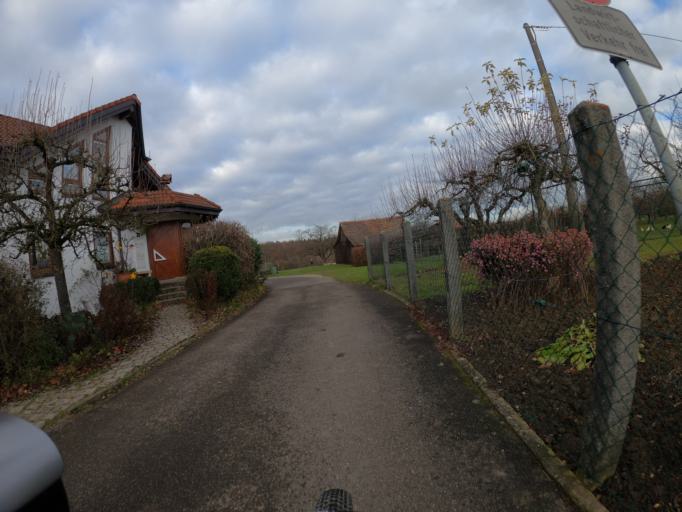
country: DE
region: Baden-Wuerttemberg
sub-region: Regierungsbezirk Stuttgart
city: Notzingen
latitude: 48.6757
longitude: 9.4706
